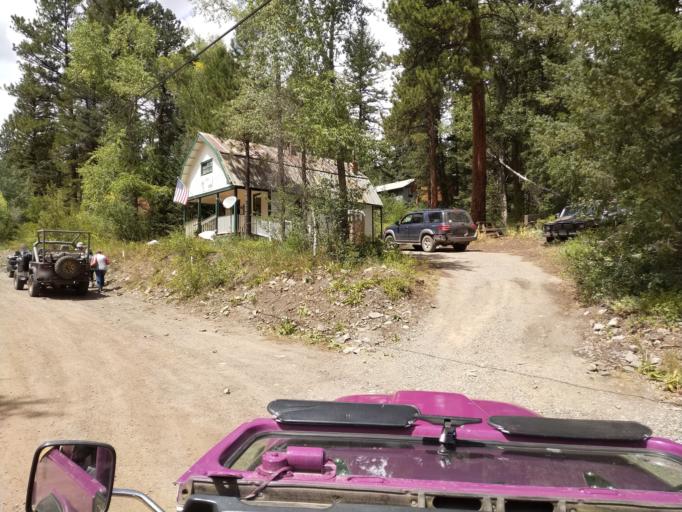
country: US
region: Colorado
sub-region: Gunnison County
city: Crested Butte
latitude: 39.0718
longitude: -107.1920
